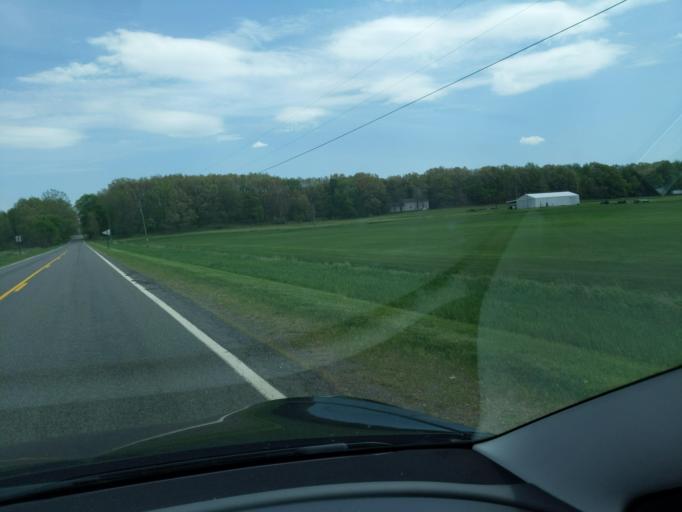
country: US
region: Michigan
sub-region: Ingham County
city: Stockbridge
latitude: 42.4832
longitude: -84.2479
